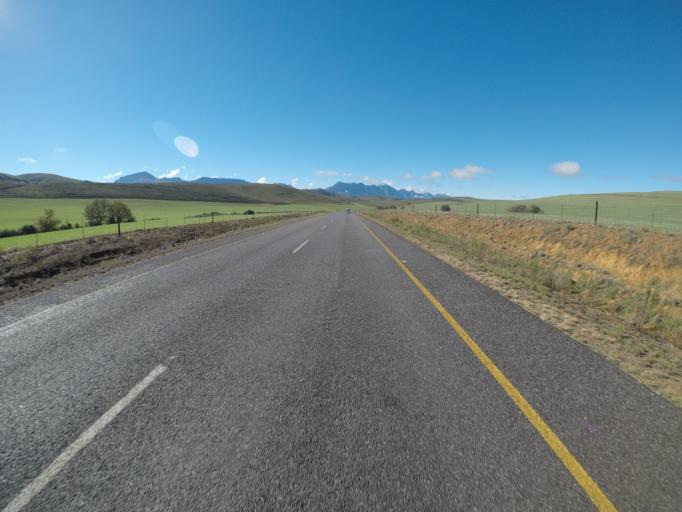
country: ZA
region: Western Cape
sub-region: Overberg District Municipality
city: Caledon
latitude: -34.0959
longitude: 19.5379
